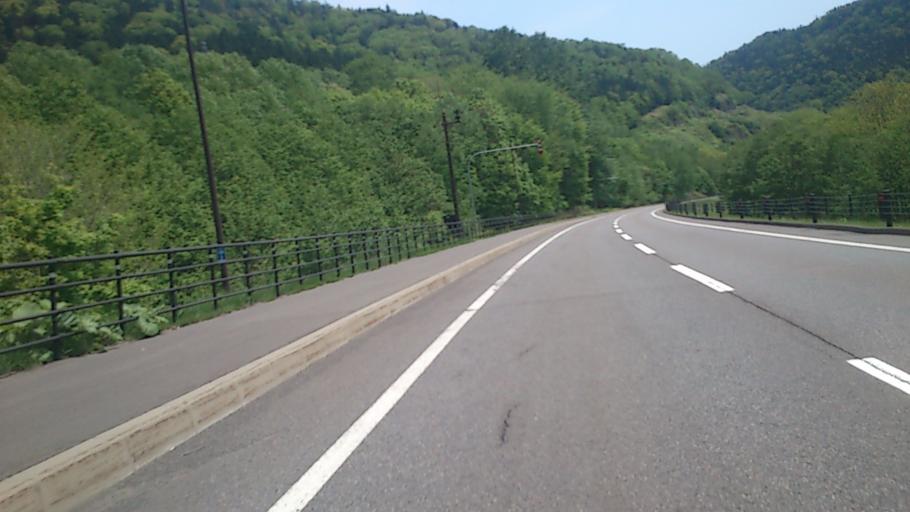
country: JP
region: Hokkaido
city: Otofuke
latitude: 43.3693
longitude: 143.2306
